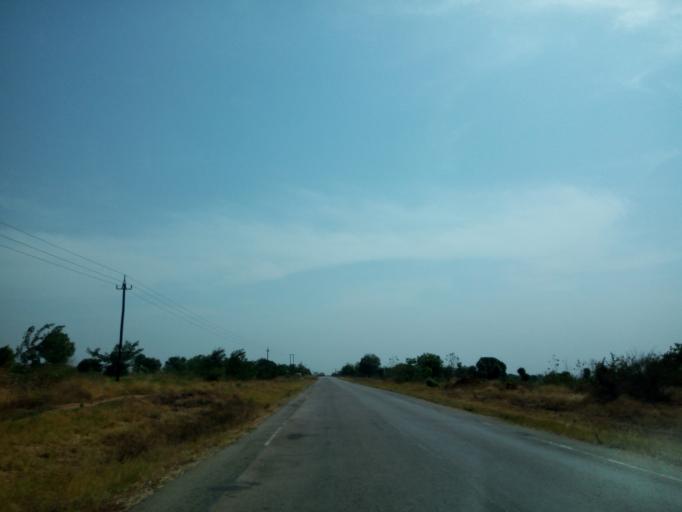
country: UG
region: Northern Region
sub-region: Nebbi District
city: Nebbi
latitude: 2.4645
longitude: 31.3108
